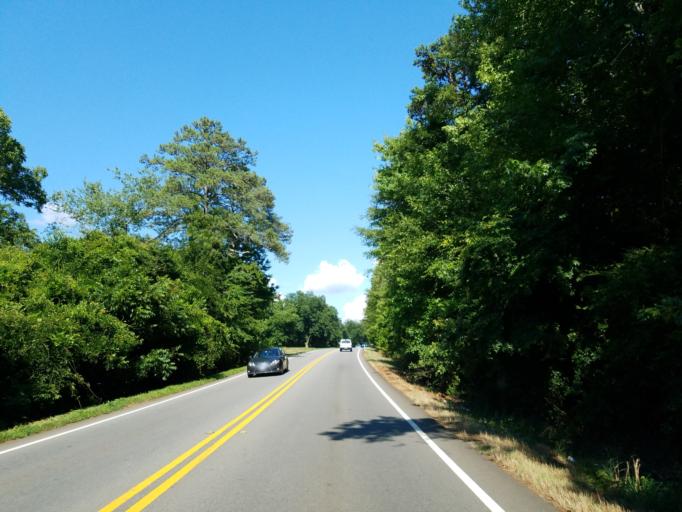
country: US
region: Georgia
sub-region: Peach County
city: Fort Valley
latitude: 32.5568
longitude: -83.8381
